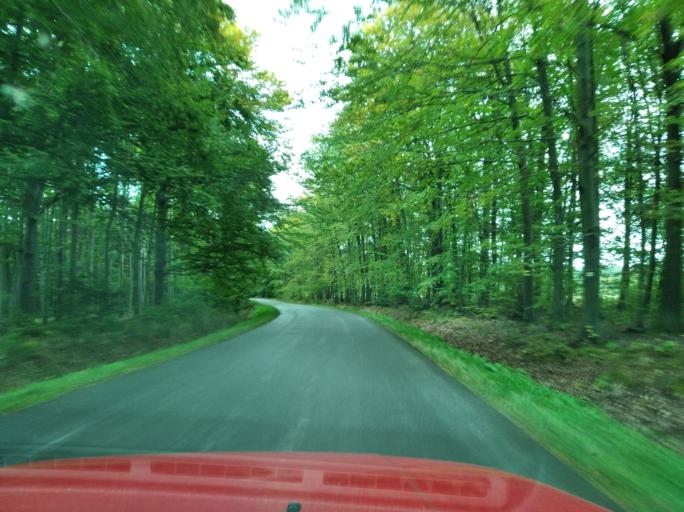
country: PL
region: Subcarpathian Voivodeship
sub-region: Powiat rzeszowski
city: Straszydle
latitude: 49.9309
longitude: 22.0014
